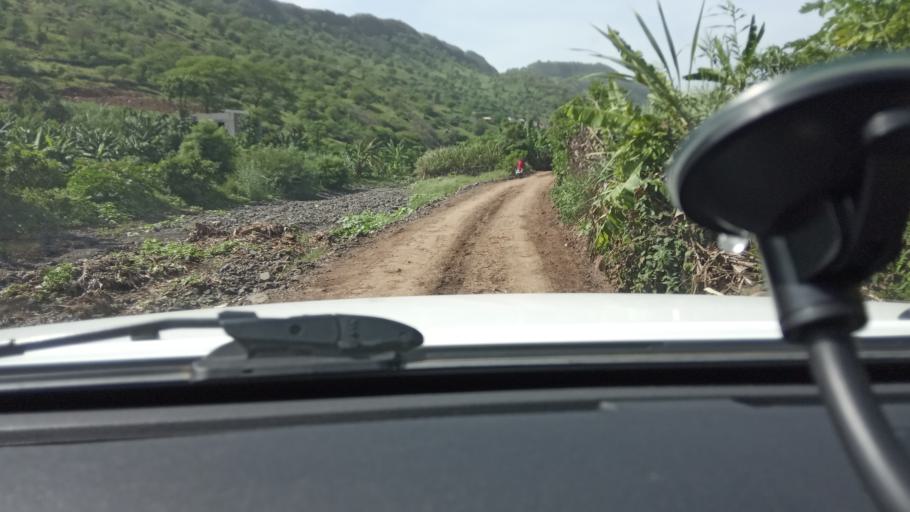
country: CV
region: Santa Cruz
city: Santa Cruz
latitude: 15.1158
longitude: -23.5499
